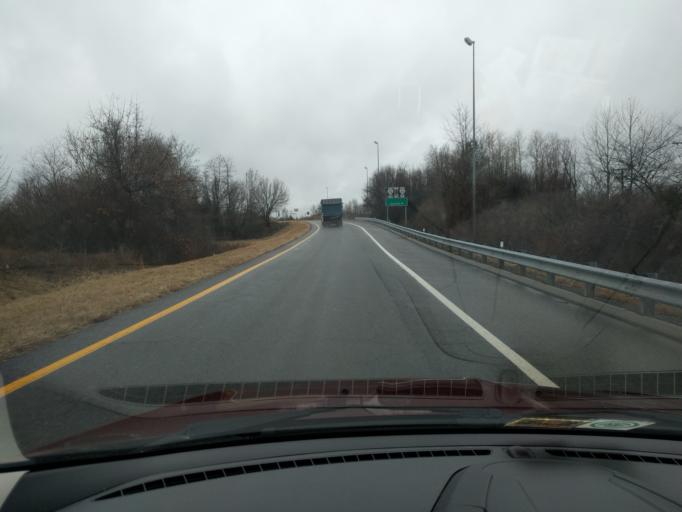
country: US
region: Virginia
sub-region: Montgomery County
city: Merrimac
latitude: 37.1662
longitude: -80.4158
